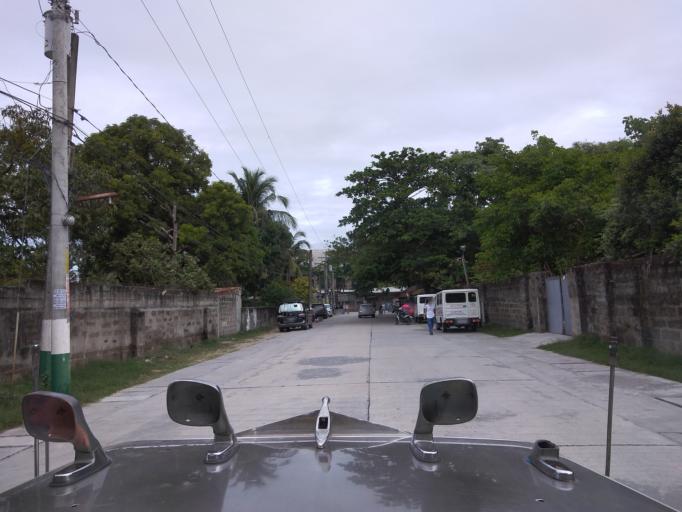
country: PH
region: Central Luzon
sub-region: Province of Pampanga
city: Mexico
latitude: 15.0632
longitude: 120.7195
